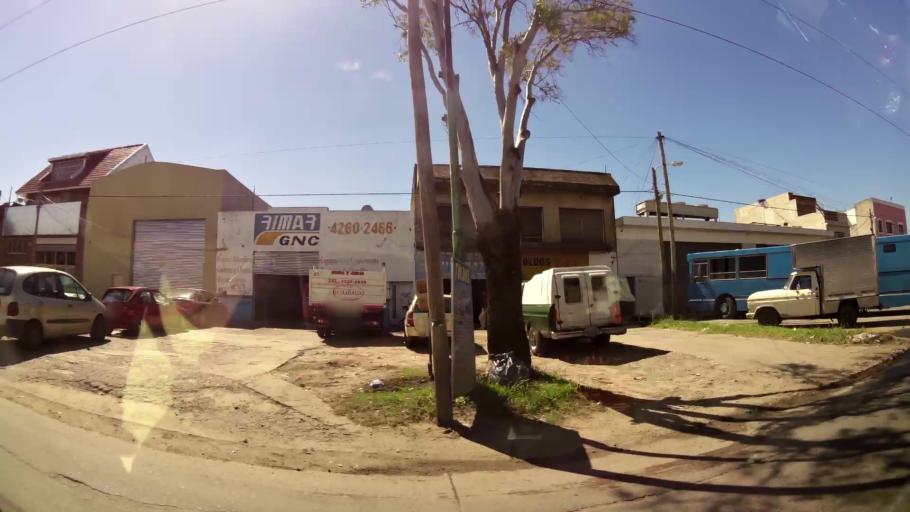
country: AR
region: Buenos Aires
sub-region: Partido de Almirante Brown
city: Adrogue
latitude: -34.7573
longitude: -58.3531
